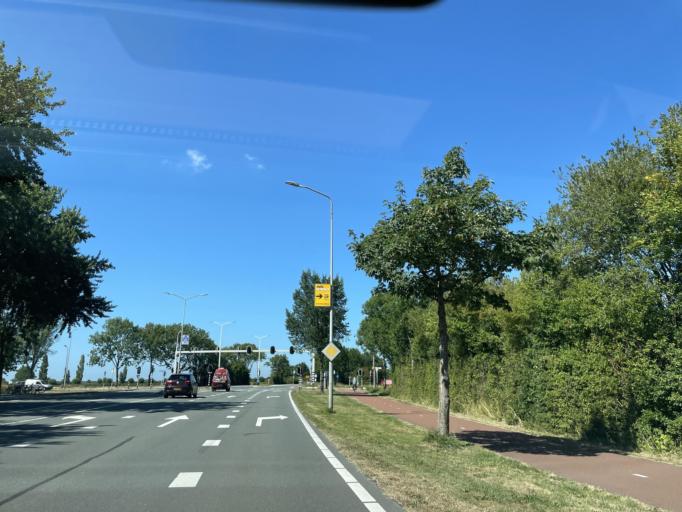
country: NL
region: Zeeland
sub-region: Gemeente Middelburg
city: Middelburg
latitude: 51.5054
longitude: 3.6019
